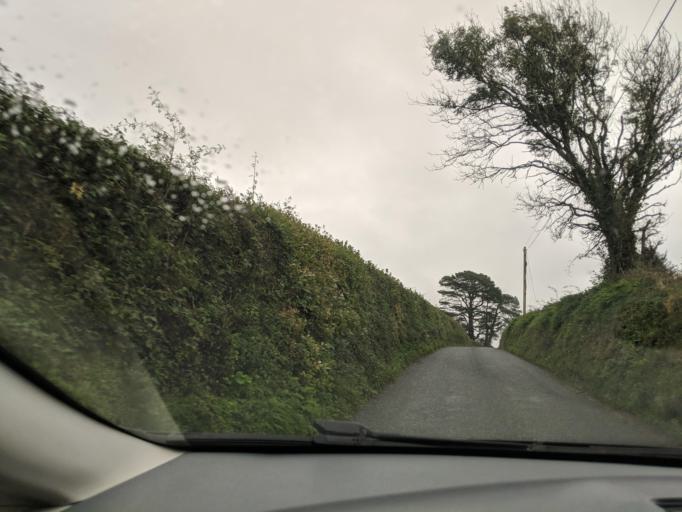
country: GB
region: England
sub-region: Cornwall
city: Saltash
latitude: 50.4507
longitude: -4.2399
